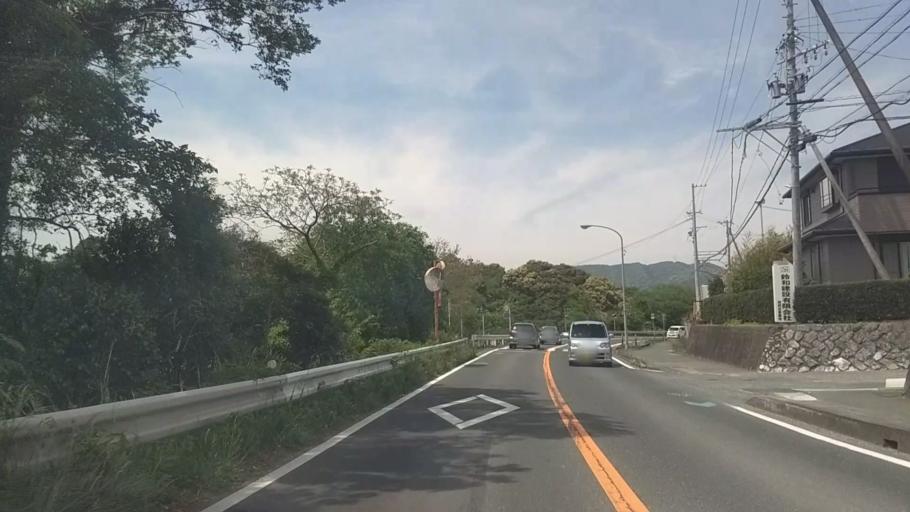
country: JP
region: Shizuoka
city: Kosai-shi
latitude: 34.7481
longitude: 137.5124
